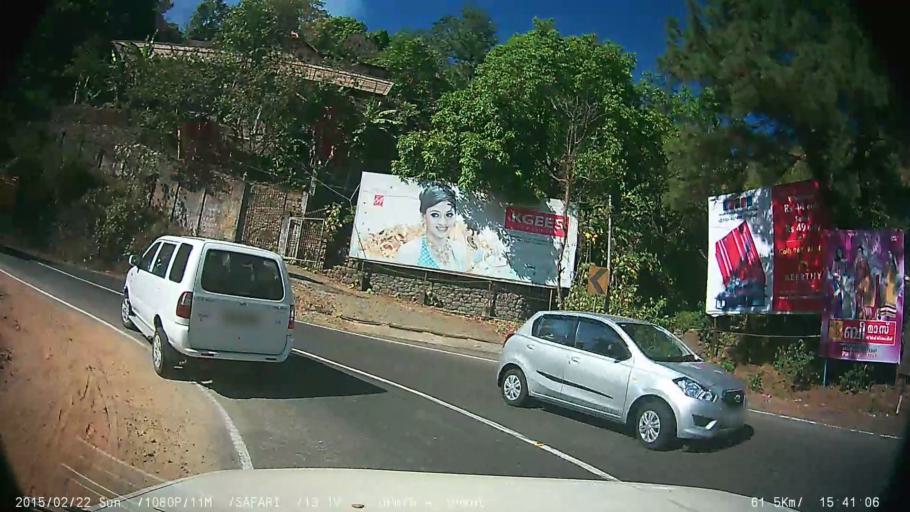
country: IN
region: Kerala
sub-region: Kottayam
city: Erattupetta
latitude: 9.5734
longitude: 76.9756
